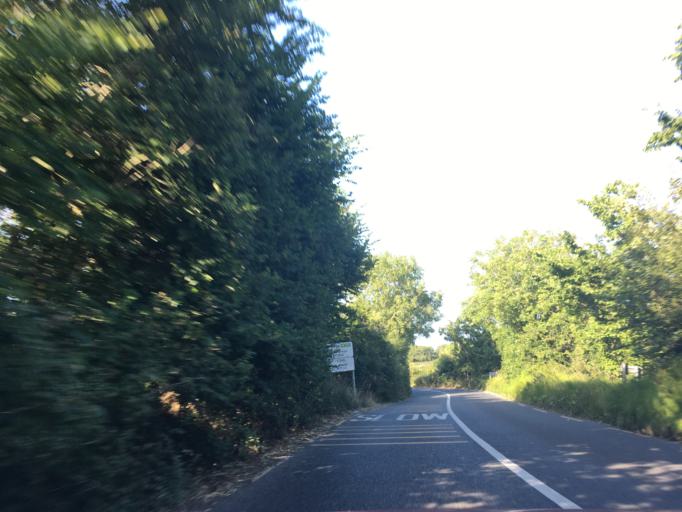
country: IE
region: Leinster
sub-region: Loch Garman
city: Loch Garman
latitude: 52.2596
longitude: -6.4838
